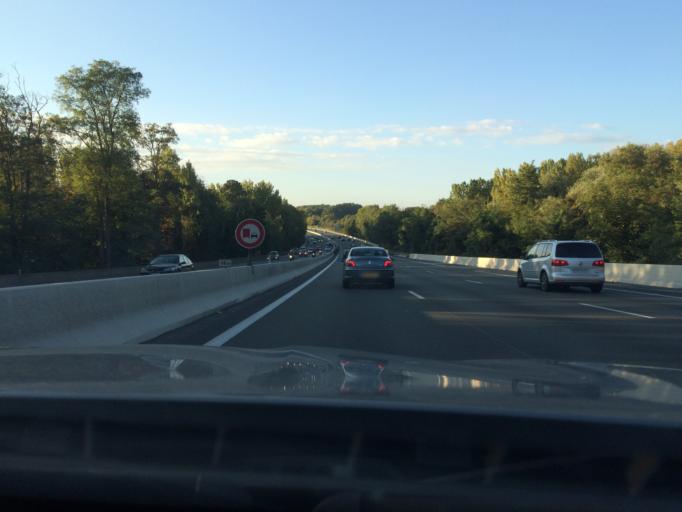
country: FR
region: Ile-de-France
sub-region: Departement de l'Essonne
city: Ormoy
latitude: 48.5755
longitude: 2.4656
